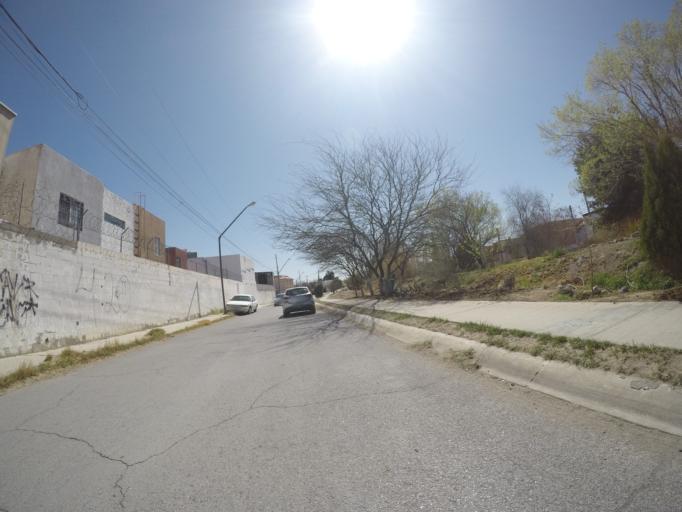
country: MX
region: Chihuahua
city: Ciudad Juarez
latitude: 31.6913
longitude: -106.4171
